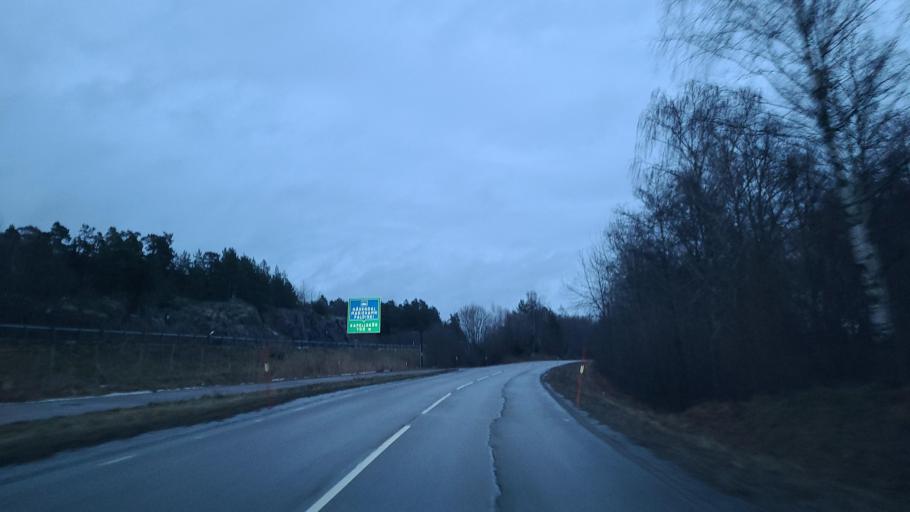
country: SE
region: Stockholm
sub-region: Norrtalje Kommun
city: Norrtalje
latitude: 59.7419
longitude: 18.6539
